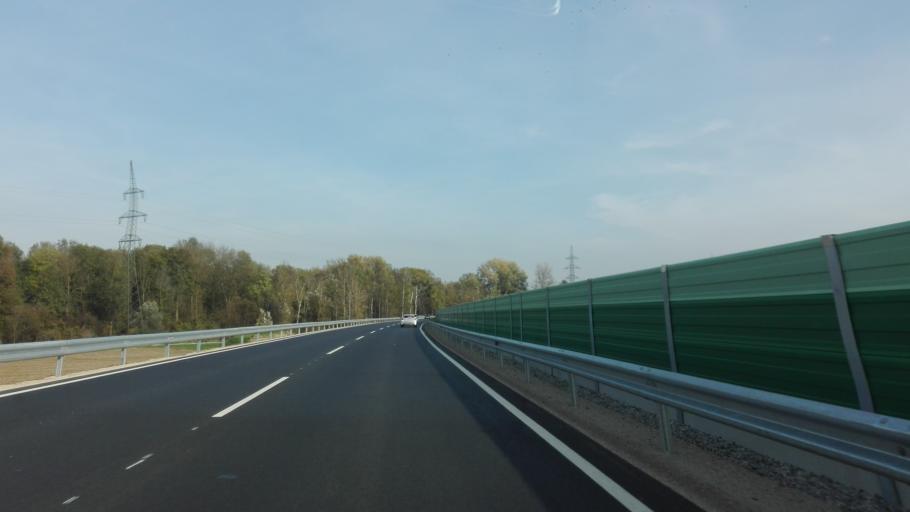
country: AT
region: Lower Austria
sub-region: Politischer Bezirk Amstetten
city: Ennsdorf
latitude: 48.2335
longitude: 14.5226
